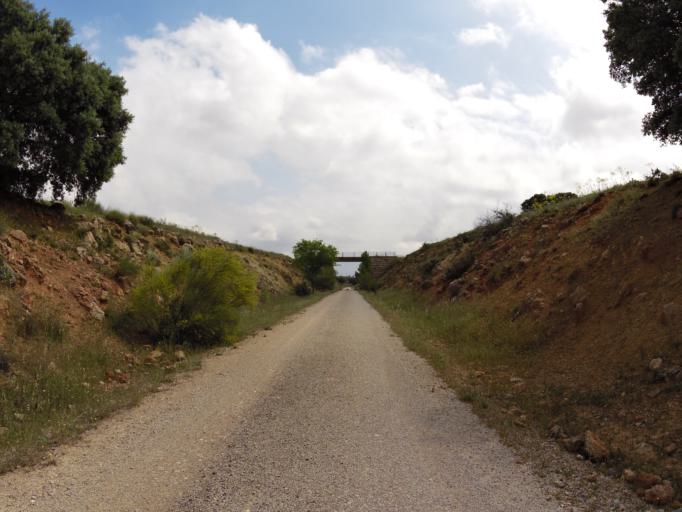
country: ES
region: Castille-La Mancha
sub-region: Provincia de Albacete
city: Robledo
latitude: 38.7723
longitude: -2.4437
